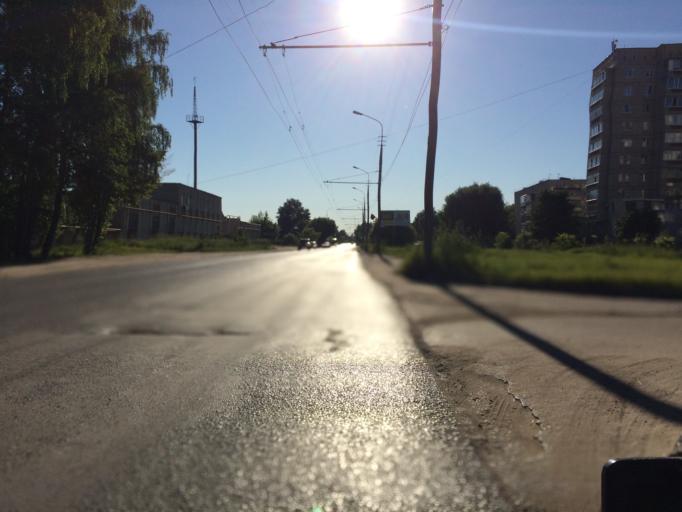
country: RU
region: Mariy-El
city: Yoshkar-Ola
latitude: 56.6527
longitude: 47.8598
